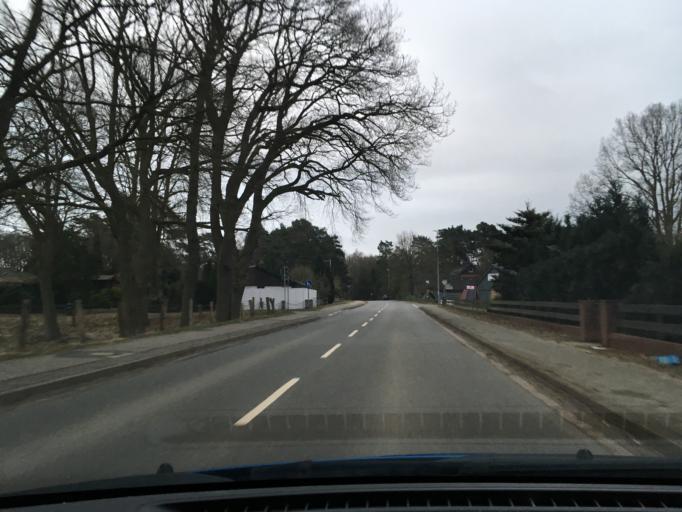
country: DE
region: Lower Saxony
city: Barum
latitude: 53.3485
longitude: 10.4141
